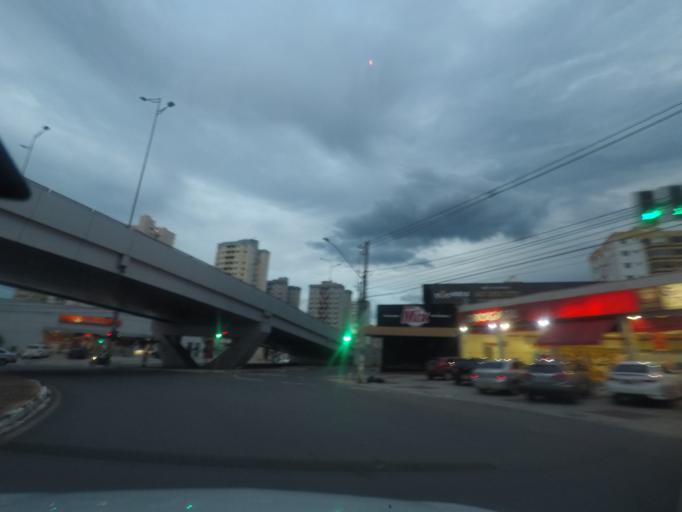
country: BR
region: Goias
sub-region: Goiania
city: Goiania
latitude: -16.7141
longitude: -49.2636
